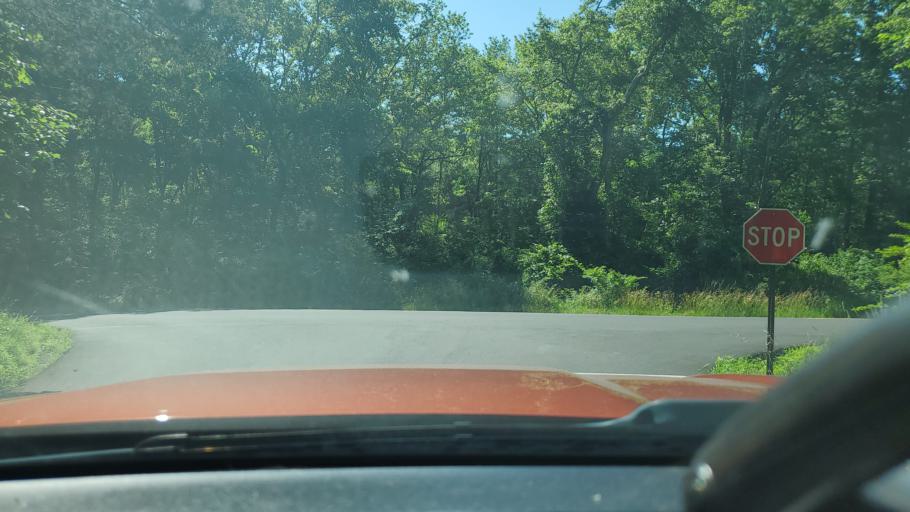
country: US
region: Pennsylvania
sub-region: Montgomery County
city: Red Hill
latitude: 40.3267
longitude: -75.5146
